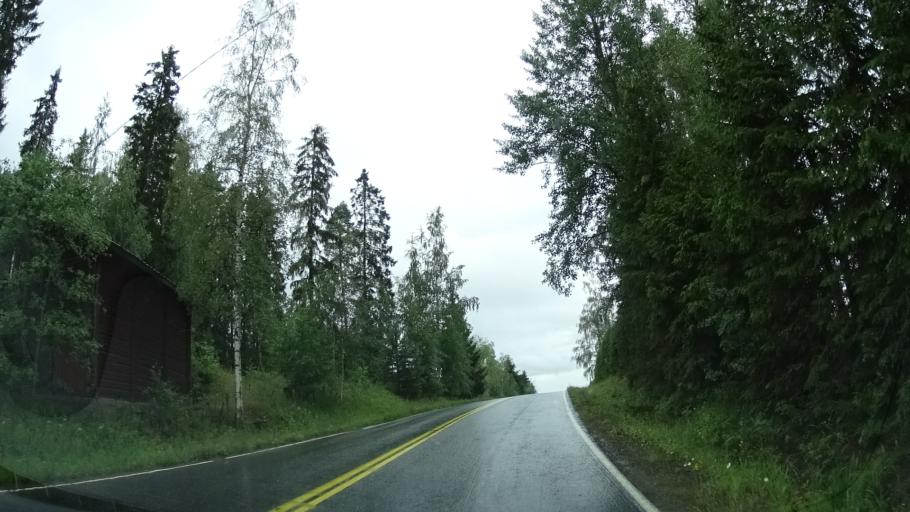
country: FI
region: Haeme
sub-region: Forssa
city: Humppila
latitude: 61.0048
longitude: 23.2523
